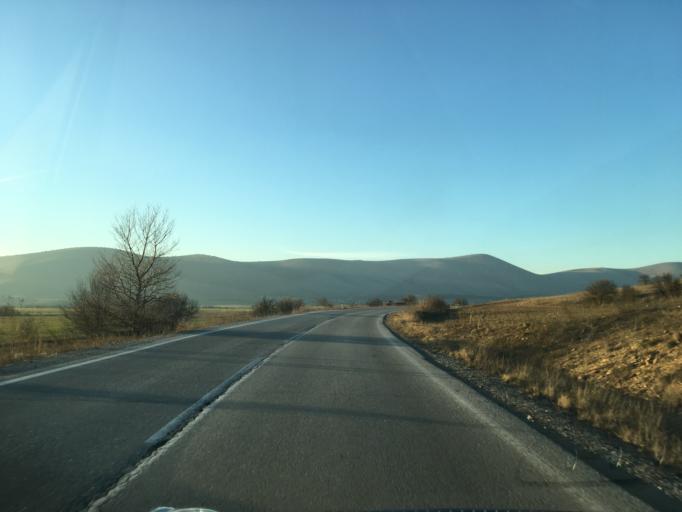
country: GR
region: West Macedonia
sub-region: Nomos Kozanis
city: Kozani
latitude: 40.3099
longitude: 21.7326
